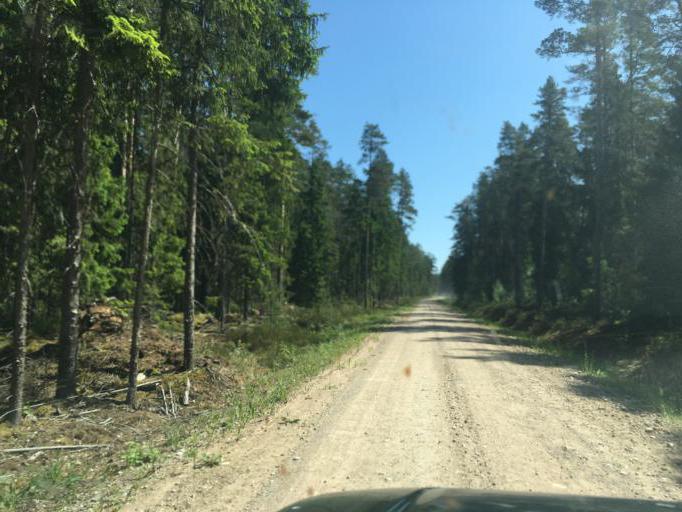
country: LV
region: Talsu Rajons
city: Valdemarpils
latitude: 57.4339
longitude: 22.6874
